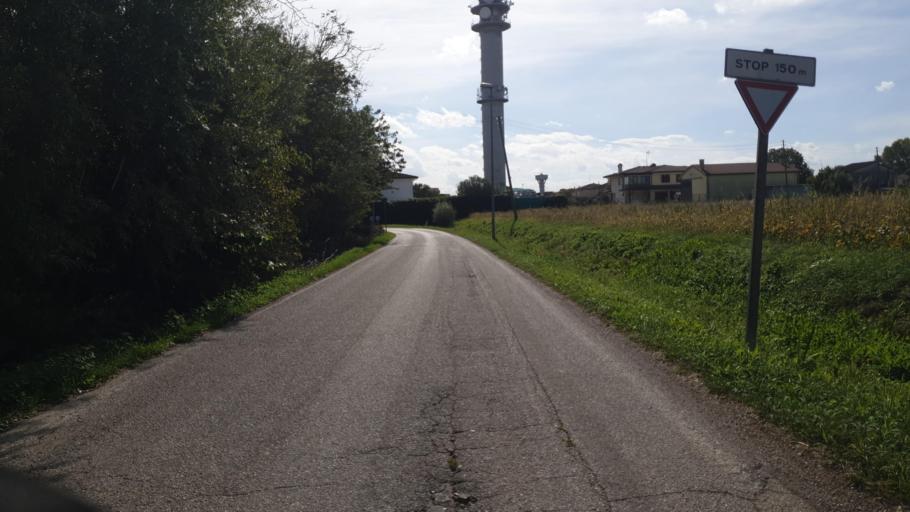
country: IT
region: Veneto
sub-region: Provincia di Padova
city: Arzergrande
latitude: 45.2757
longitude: 12.0555
